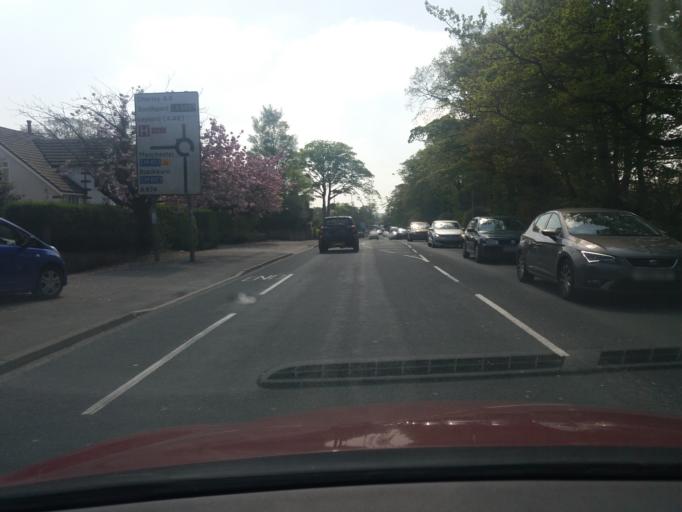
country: GB
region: England
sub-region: Lancashire
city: Chorley
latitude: 53.6701
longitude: -2.6323
